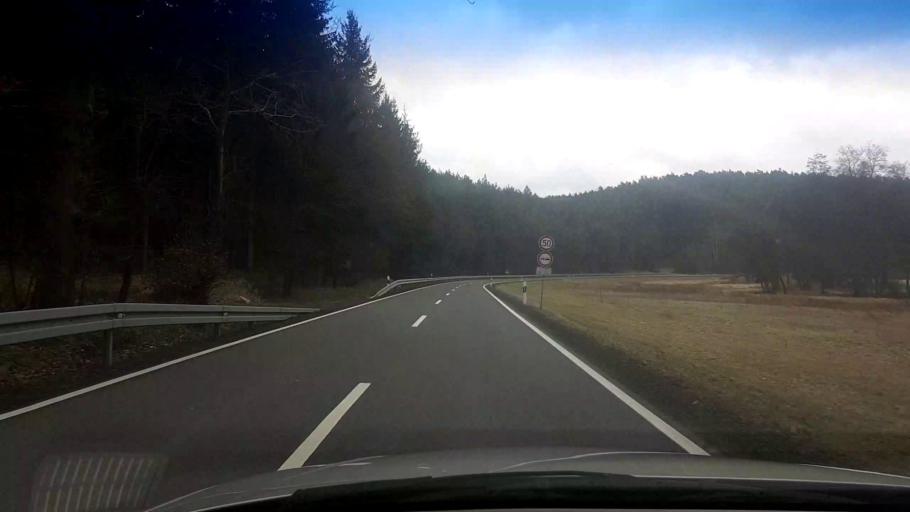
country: DE
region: Bavaria
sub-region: Regierungsbezirk Unterfranken
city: Eltmann
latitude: 49.9375
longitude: 10.6383
